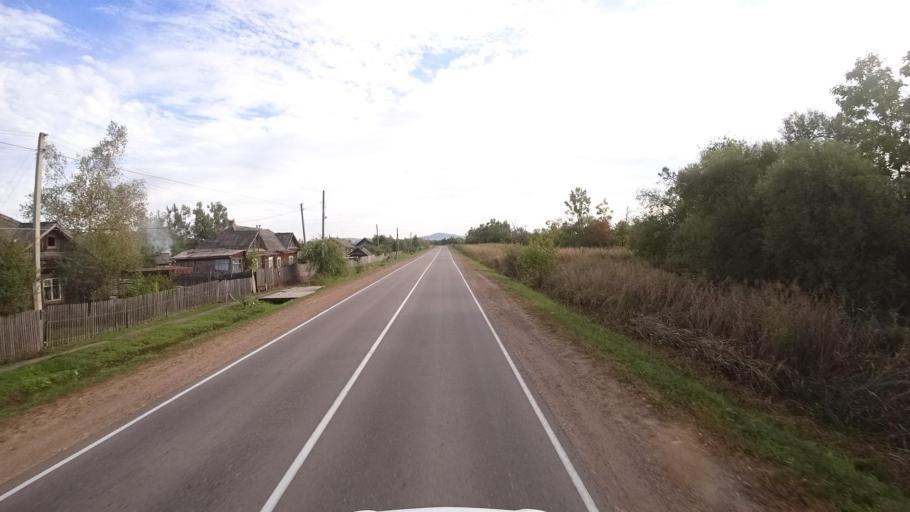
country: RU
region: Primorskiy
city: Dostoyevka
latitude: 44.2879
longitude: 133.4263
